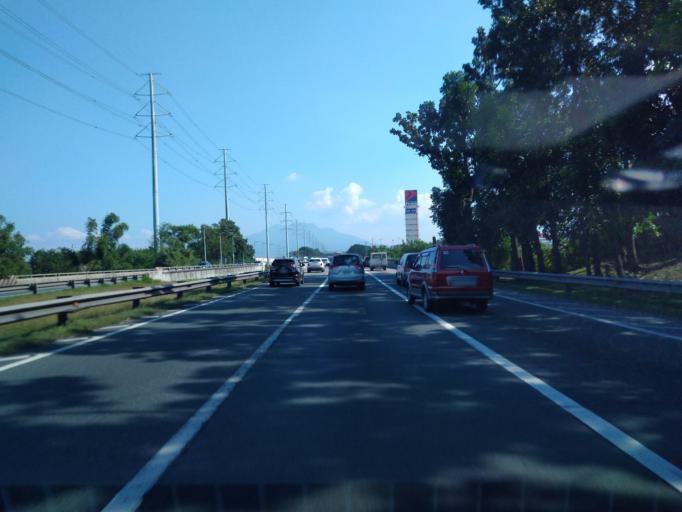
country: PH
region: Calabarzon
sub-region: Province of Laguna
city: Cabuyao
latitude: 14.2377
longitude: 121.1136
